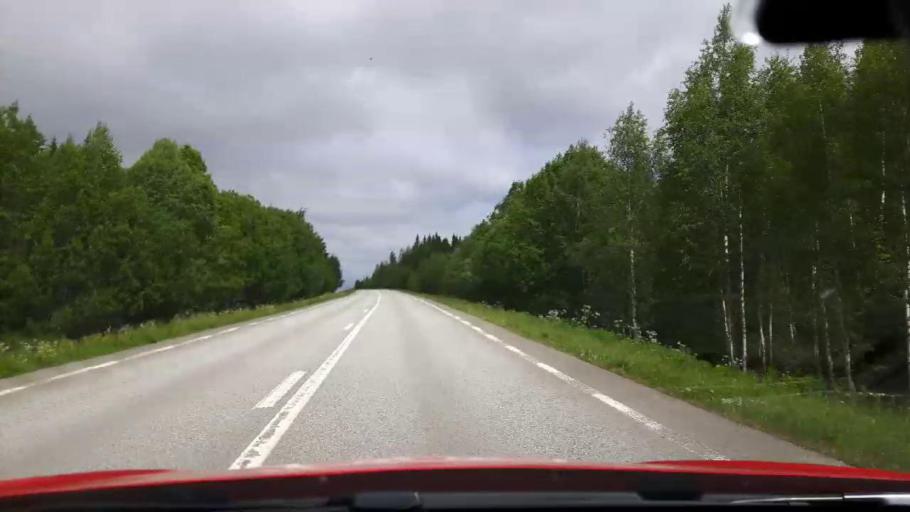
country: SE
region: Jaemtland
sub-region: Krokoms Kommun
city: Krokom
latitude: 63.4986
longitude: 14.5115
